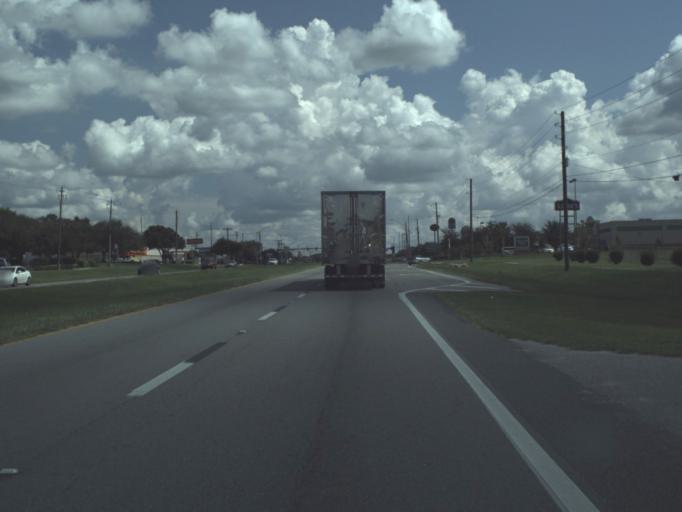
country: US
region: Florida
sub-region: Polk County
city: Auburndale
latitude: 28.0564
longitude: -81.8220
